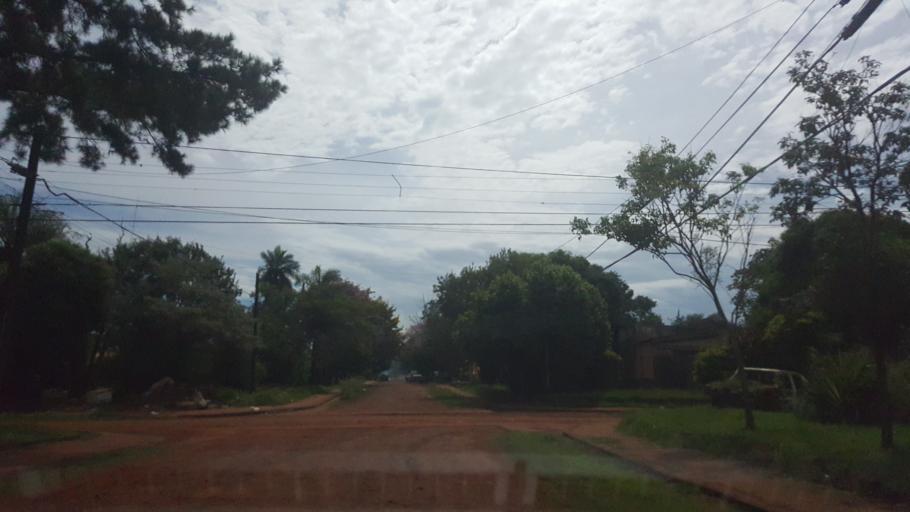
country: AR
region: Misiones
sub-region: Departamento de Capital
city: Posadas
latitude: -27.3973
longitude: -55.9183
